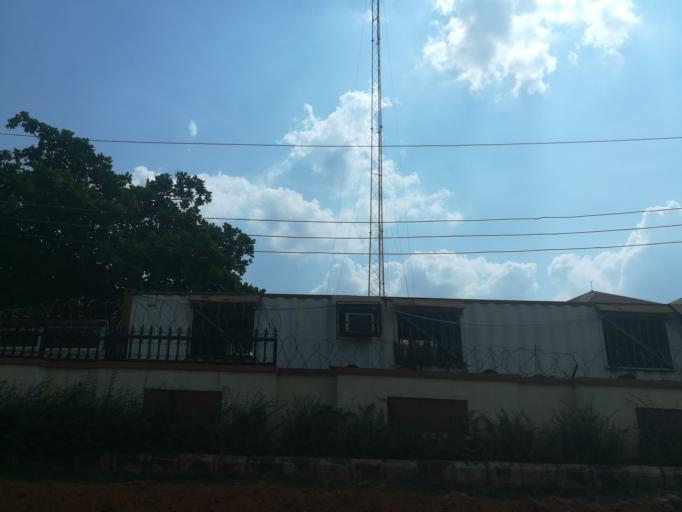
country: NG
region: Abuja Federal Capital Territory
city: Abuja
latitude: 9.0512
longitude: 7.4468
